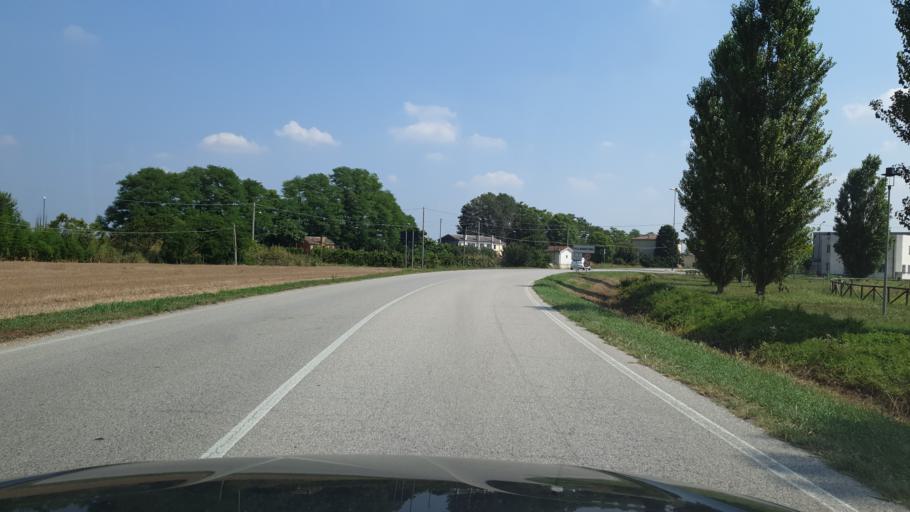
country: IT
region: Veneto
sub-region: Provincia di Rovigo
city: Villamarzana
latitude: 45.0194
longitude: 11.6813
